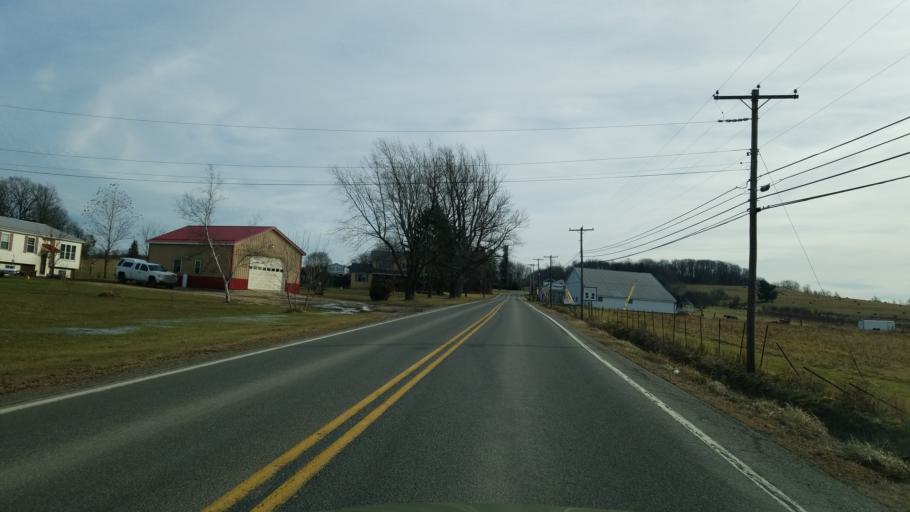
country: US
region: Pennsylvania
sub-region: Indiana County
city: Johnsonburg
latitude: 40.9240
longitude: -78.8680
